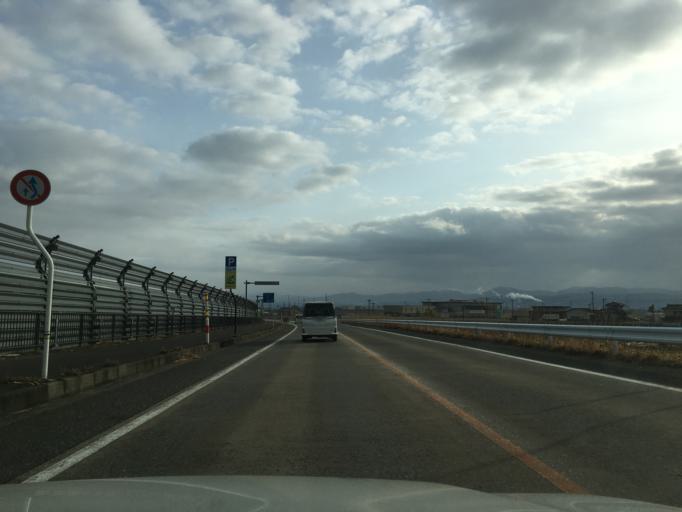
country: JP
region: Yamagata
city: Sakata
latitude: 38.8274
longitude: 139.8428
